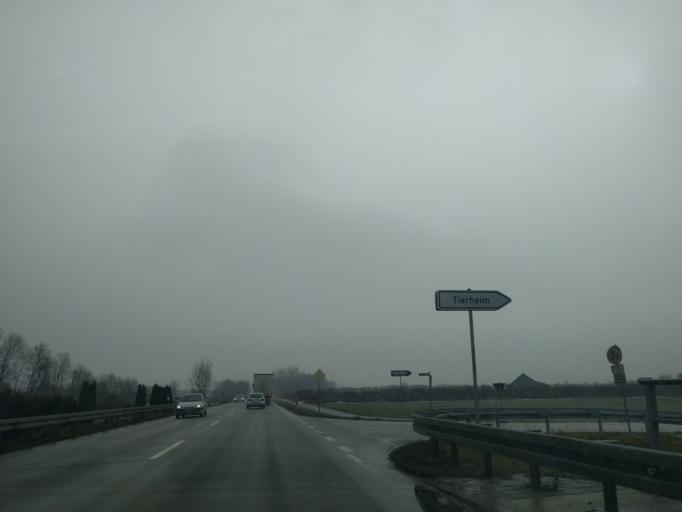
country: DE
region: Bavaria
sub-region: Lower Bavaria
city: Plattling
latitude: 48.7626
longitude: 12.8974
